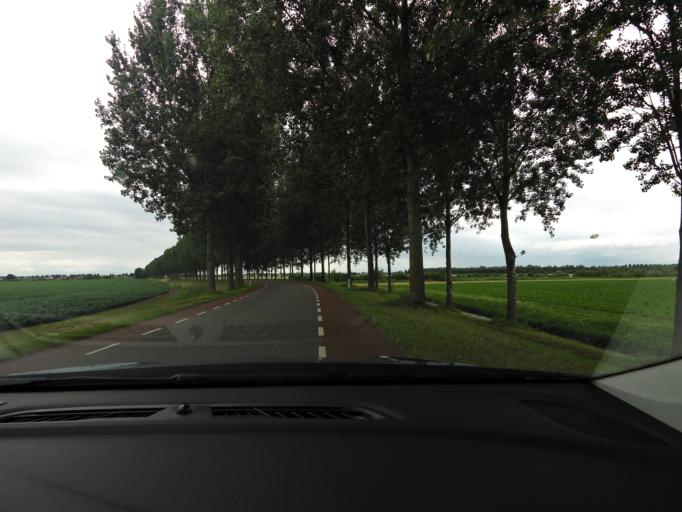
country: NL
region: South Holland
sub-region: Gemeente Strijen
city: Strijen
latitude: 51.7391
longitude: 4.5790
